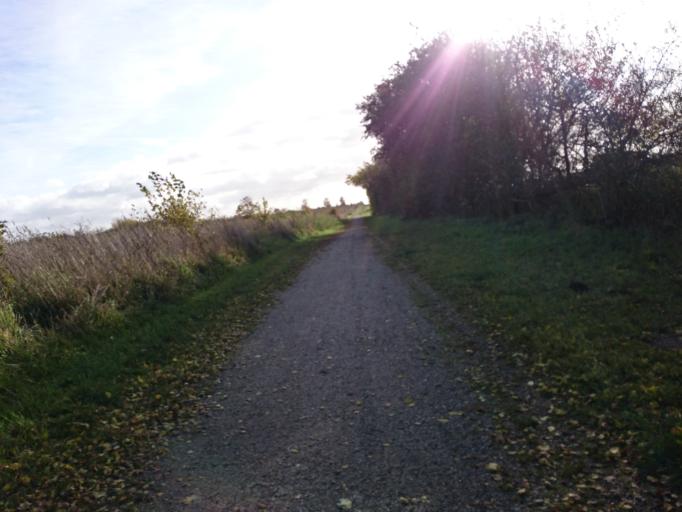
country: DK
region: South Denmark
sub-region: Odense Kommune
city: Hojby
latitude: 55.3277
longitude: 10.4331
